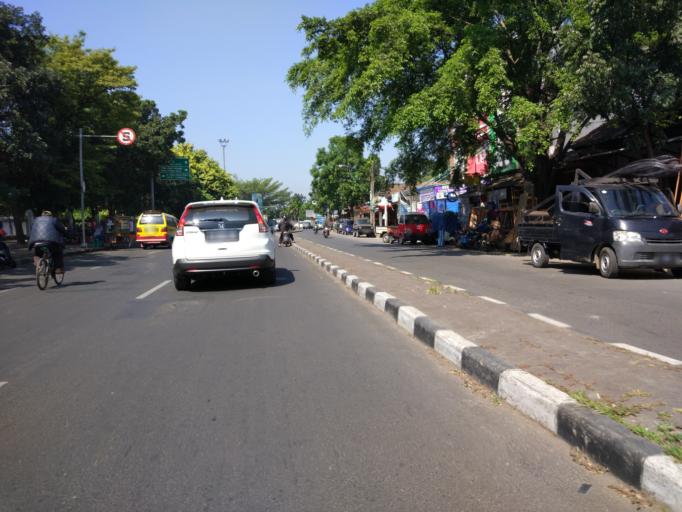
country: ID
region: West Java
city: Bandung
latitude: -6.9360
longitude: 107.6031
